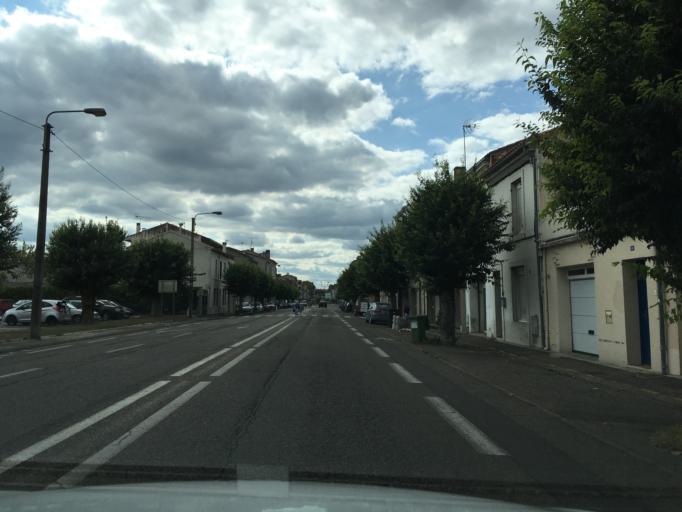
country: FR
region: Aquitaine
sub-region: Departement du Lot-et-Garonne
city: Agen
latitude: 44.2064
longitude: 0.6346
